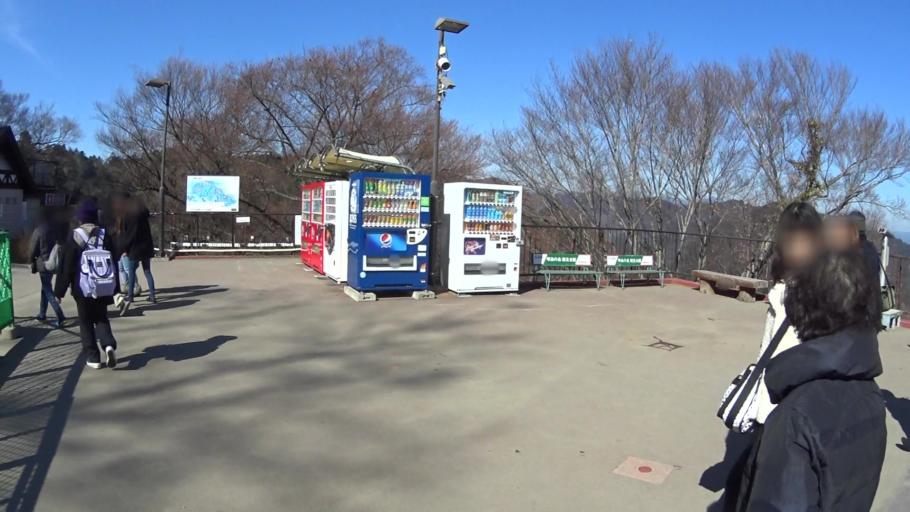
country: JP
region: Tokyo
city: Hachioji
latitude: 35.6315
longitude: 139.2551
